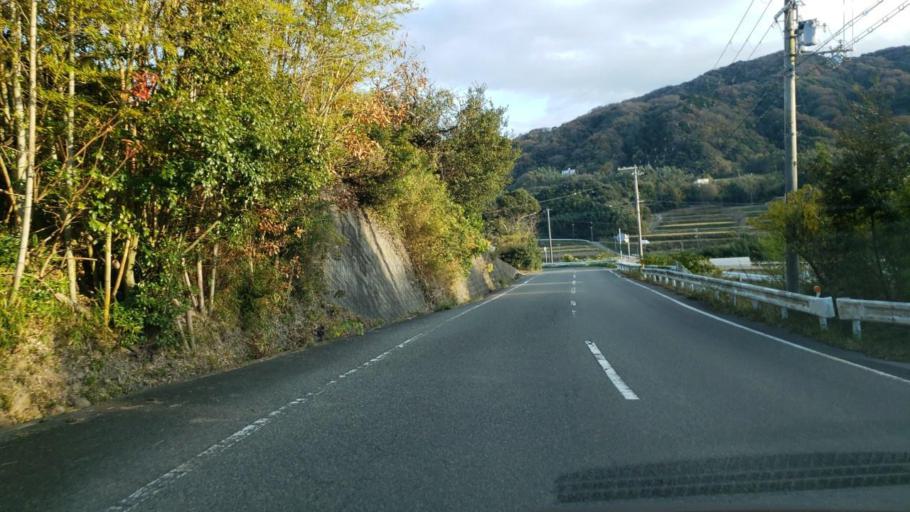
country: JP
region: Hyogo
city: Akashi
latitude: 34.5297
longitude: 134.9606
